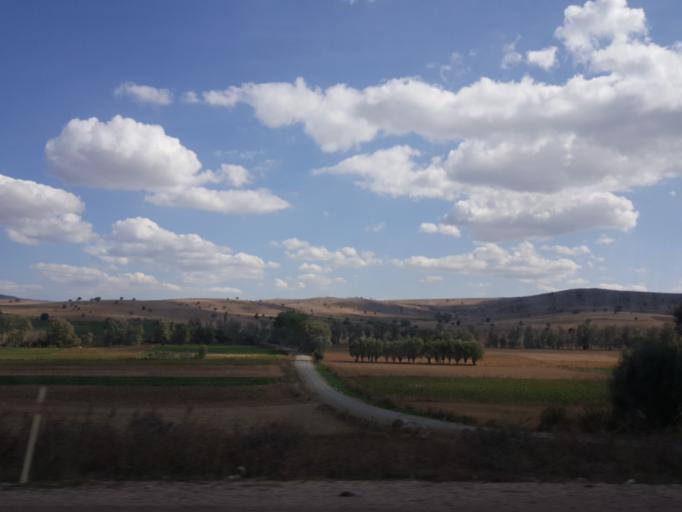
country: TR
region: Tokat
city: Camlibel
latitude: 40.1765
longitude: 36.4431
